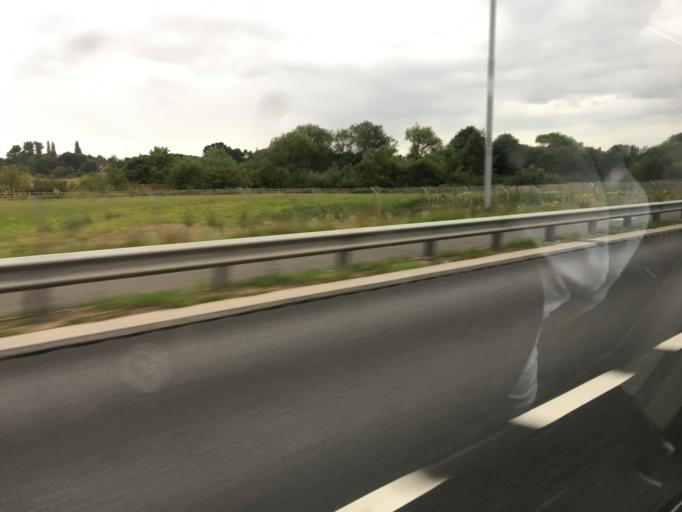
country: GB
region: England
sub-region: Coventry
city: Coventry
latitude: 52.3773
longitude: -1.4912
